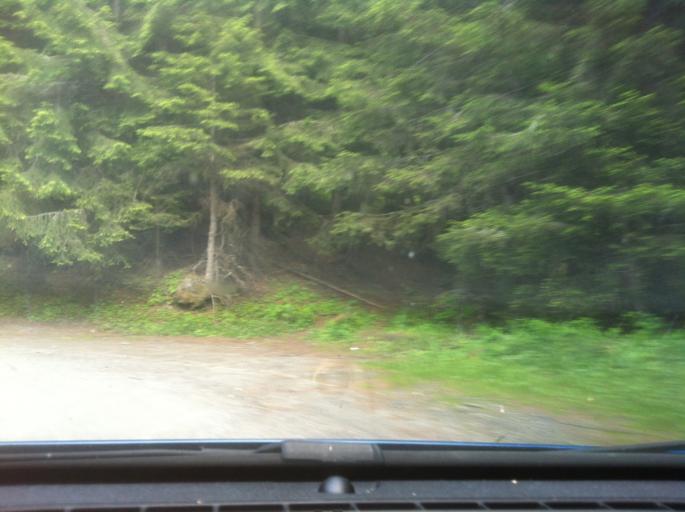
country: IT
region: Aosta Valley
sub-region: Valle d'Aosta
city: Saint Marcel
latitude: 45.7057
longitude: 7.4703
